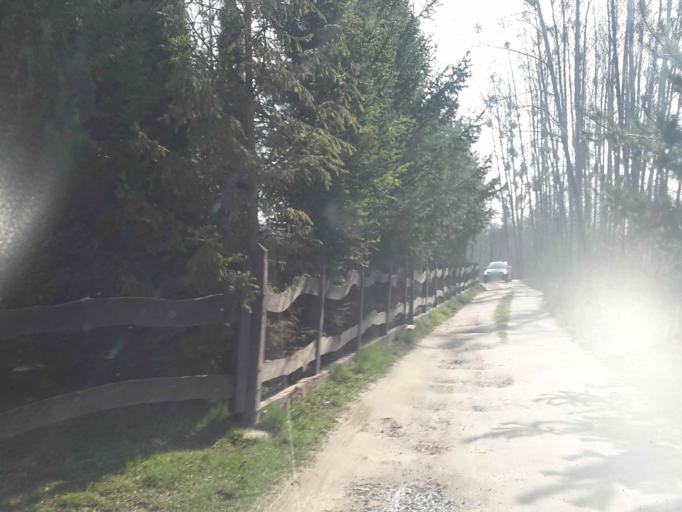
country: PL
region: Kujawsko-Pomorskie
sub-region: Powiat brodnicki
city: Brodnica
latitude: 53.3228
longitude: 19.3669
